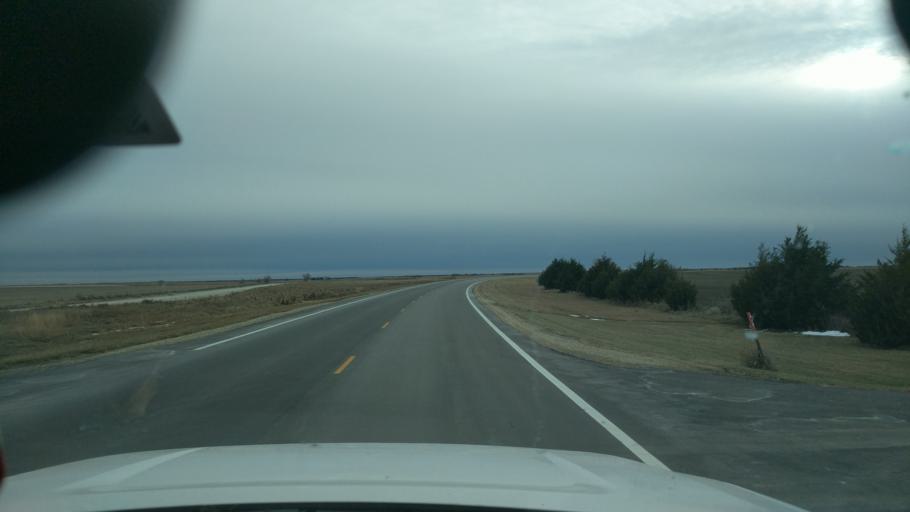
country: US
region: Kansas
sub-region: Geary County
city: Junction City
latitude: 38.8411
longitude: -96.8532
